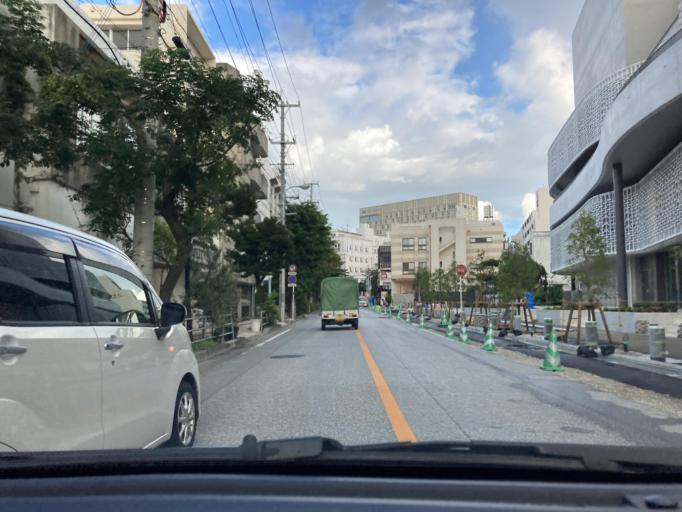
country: JP
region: Okinawa
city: Naha-shi
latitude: 26.2170
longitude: 127.6825
